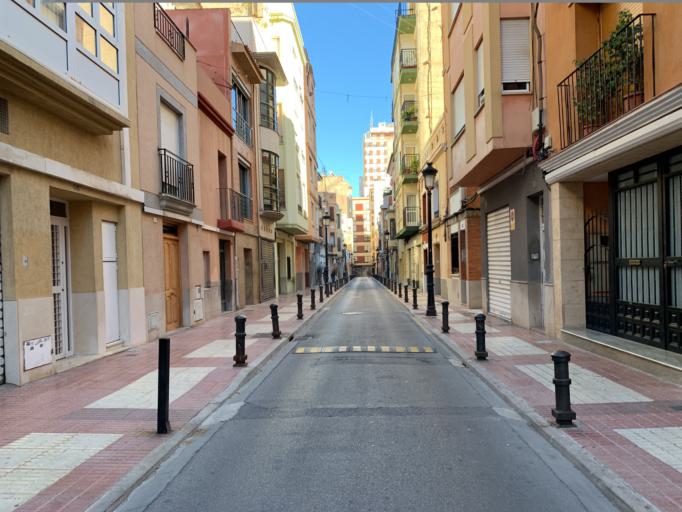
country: ES
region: Valencia
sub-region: Provincia de Castello
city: Castello de la Plana
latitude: 39.9852
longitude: -0.0427
